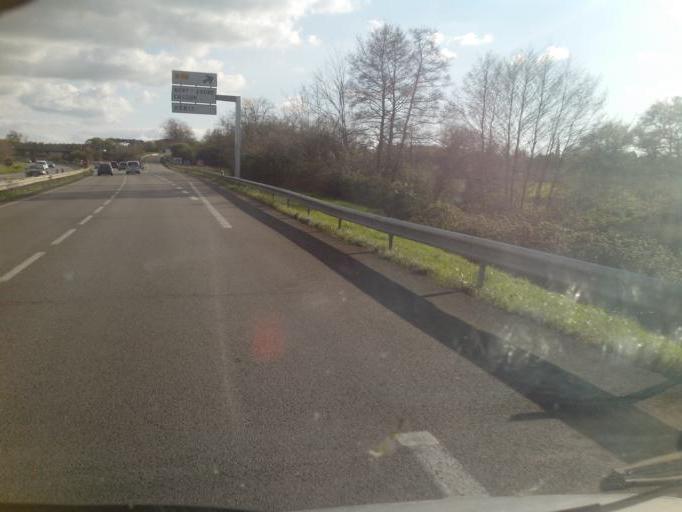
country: FR
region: Pays de la Loire
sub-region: Departement de la Loire-Atlantique
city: Heric
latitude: 47.4192
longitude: -1.6413
